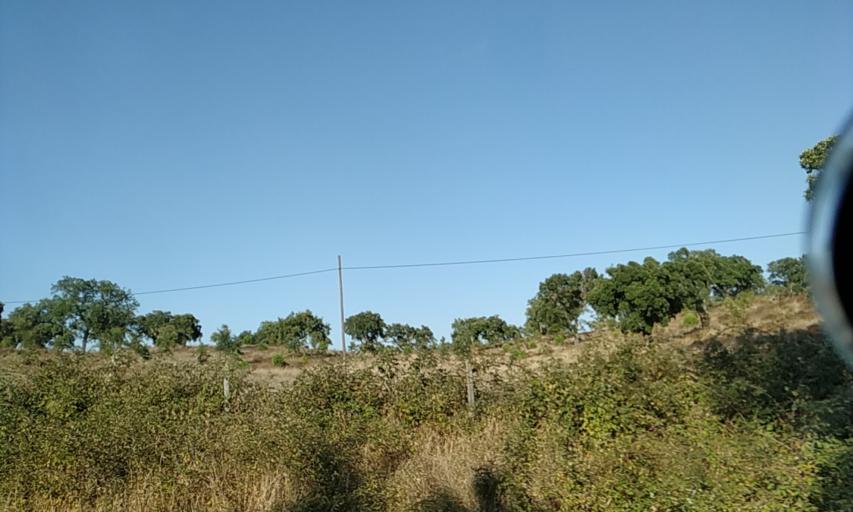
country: PT
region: Santarem
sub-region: Almeirim
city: Fazendas de Almeirim
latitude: 39.0726
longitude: -8.5657
